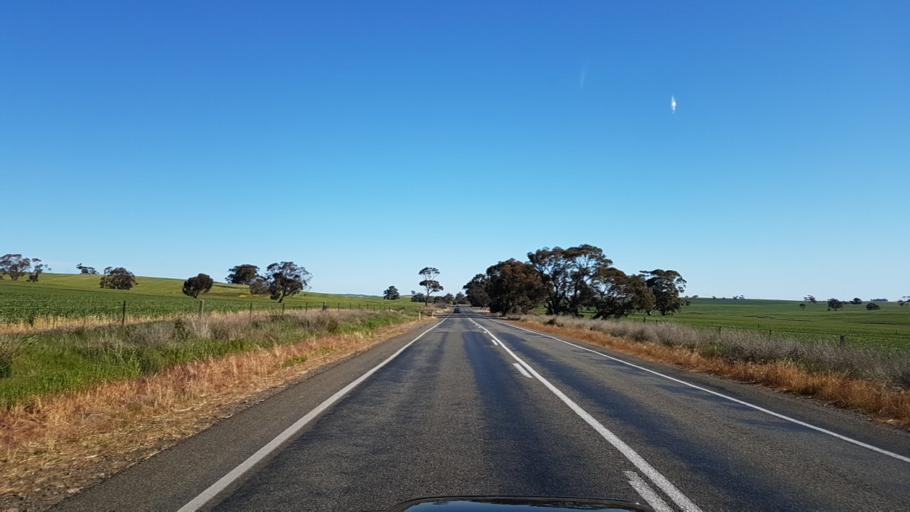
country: AU
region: South Australia
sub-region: Clare and Gilbert Valleys
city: Clare
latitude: -34.0444
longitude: 138.7992
